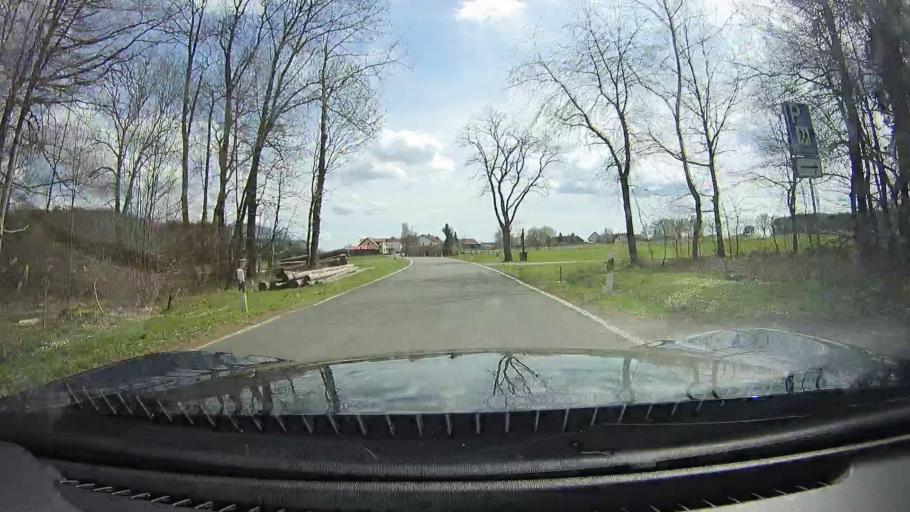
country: DE
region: Bavaria
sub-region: Regierungsbezirk Unterfranken
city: Kirchzell
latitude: 49.6256
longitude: 9.1075
